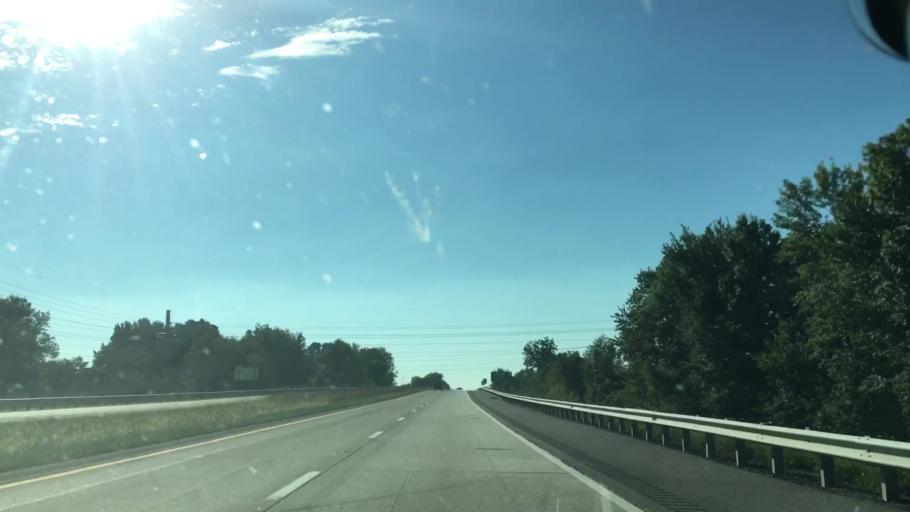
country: US
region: Kentucky
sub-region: Daviess County
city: Owensboro
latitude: 37.7663
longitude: -87.1729
